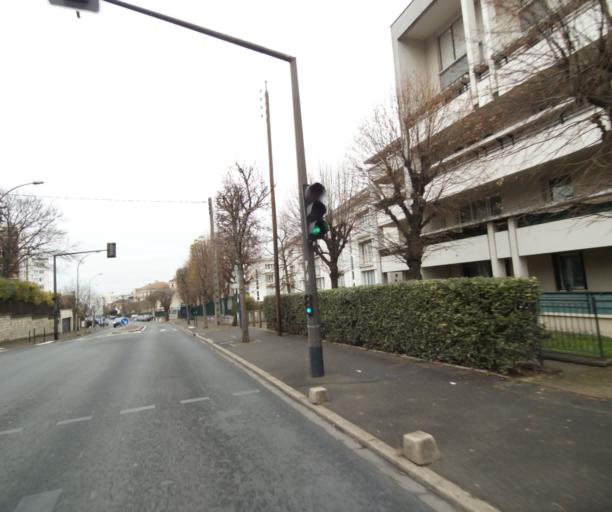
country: FR
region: Ile-de-France
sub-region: Departement des Hauts-de-Seine
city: Rueil-Malmaison
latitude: 48.8673
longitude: 2.1985
